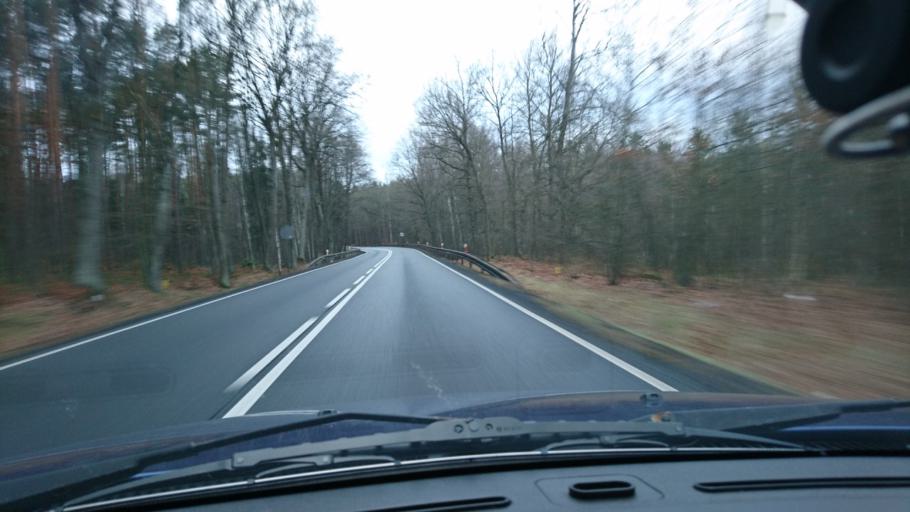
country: PL
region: Opole Voivodeship
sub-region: Powiat oleski
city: Olesno
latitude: 50.9358
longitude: 18.3307
